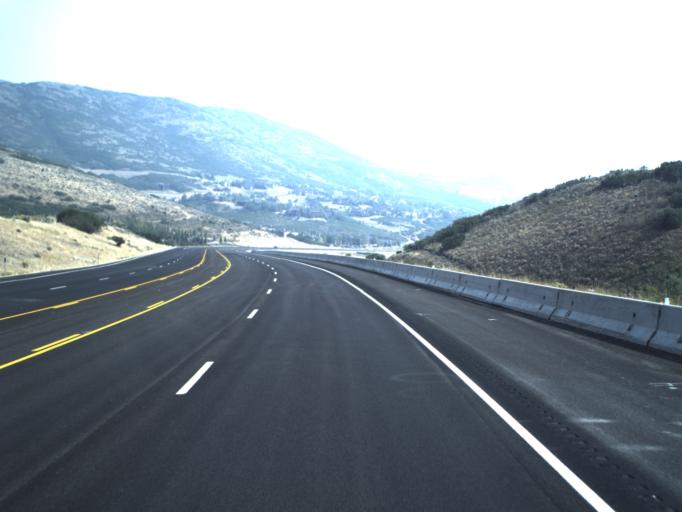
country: US
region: Utah
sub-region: Summit County
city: Park City
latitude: 40.6706
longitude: -111.4260
